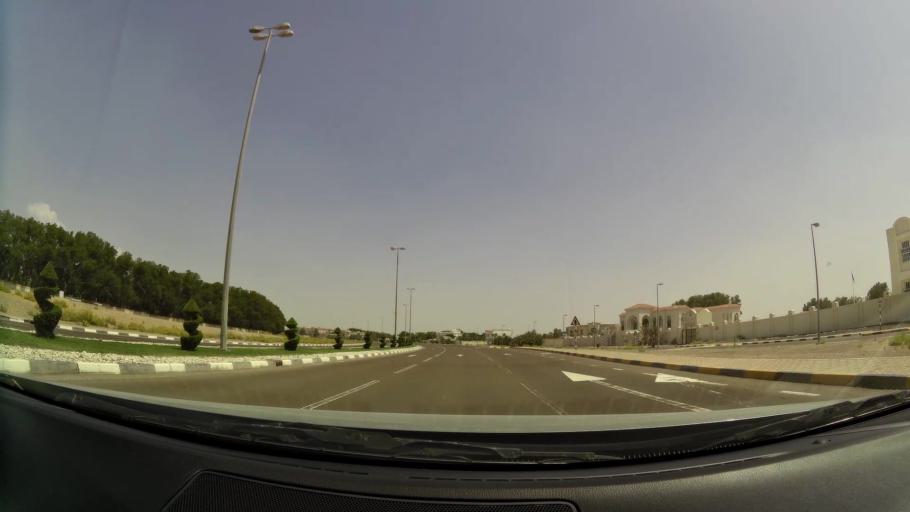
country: AE
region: Abu Dhabi
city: Al Ain
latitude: 24.2516
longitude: 55.6943
